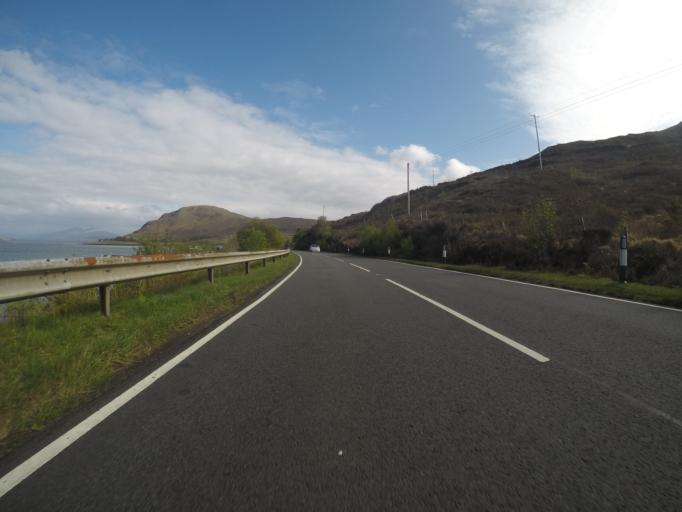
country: GB
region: Scotland
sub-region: Highland
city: Portree
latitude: 57.2731
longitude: -5.9997
